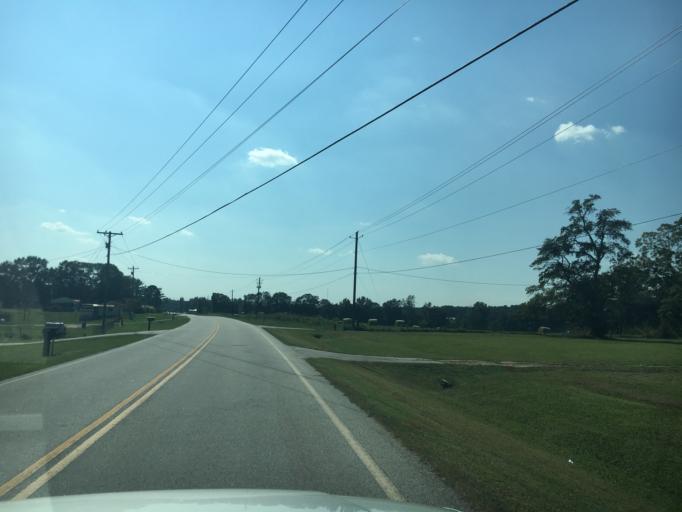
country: US
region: Georgia
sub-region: Franklin County
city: Gumlog
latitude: 34.4604
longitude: -83.0830
